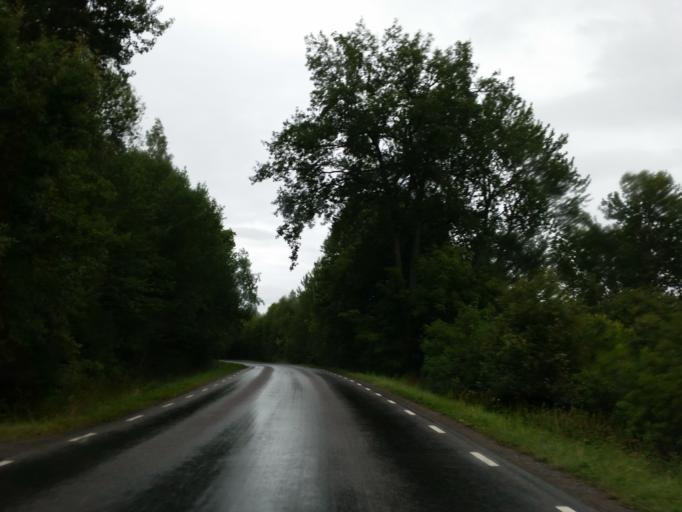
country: SE
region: Uppsala
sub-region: Habo Kommun
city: Balsta
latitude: 59.6463
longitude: 17.4609
